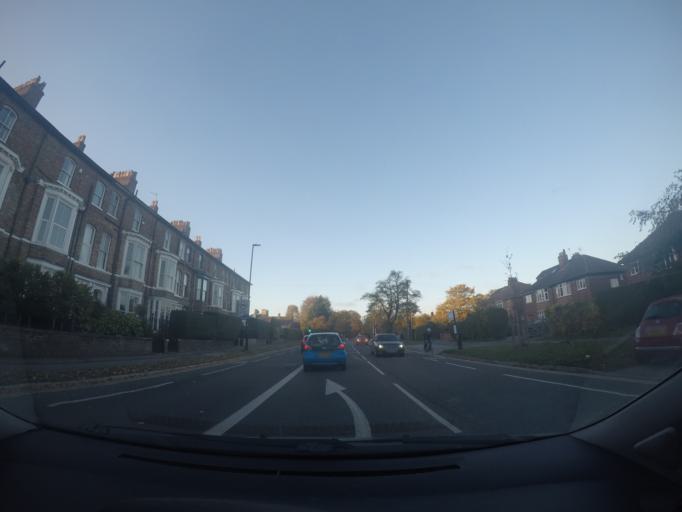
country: GB
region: England
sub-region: City of York
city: Fulford
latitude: 53.9401
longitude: -1.0742
